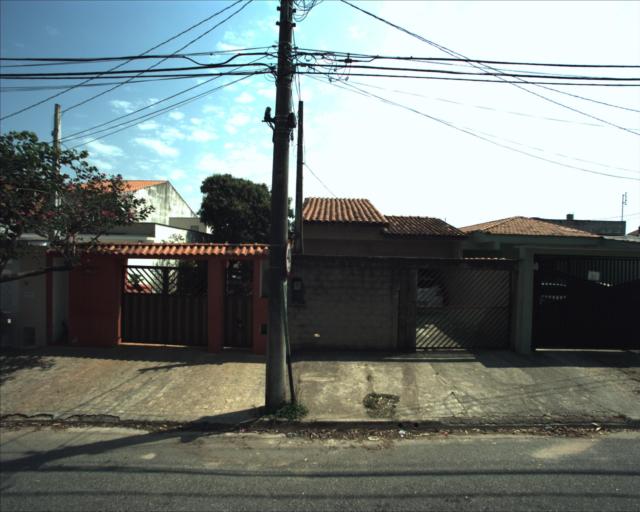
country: BR
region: Sao Paulo
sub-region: Sorocaba
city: Sorocaba
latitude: -23.4376
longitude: -47.4851
